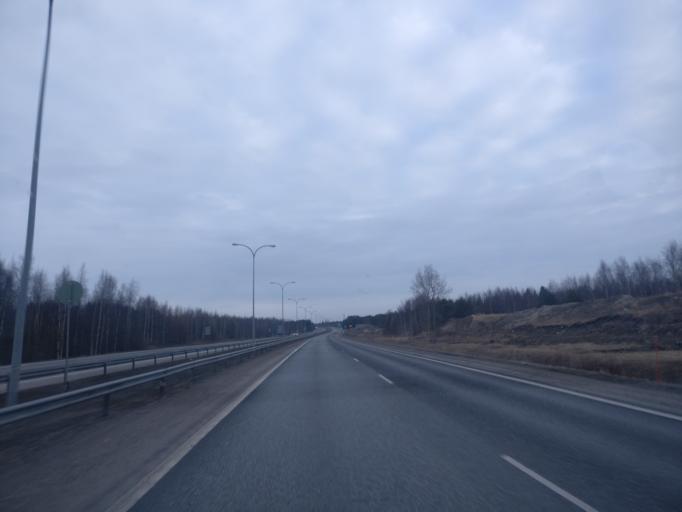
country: FI
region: Northern Ostrobothnia
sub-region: Oulu
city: Kempele
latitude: 64.9666
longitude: 25.5139
